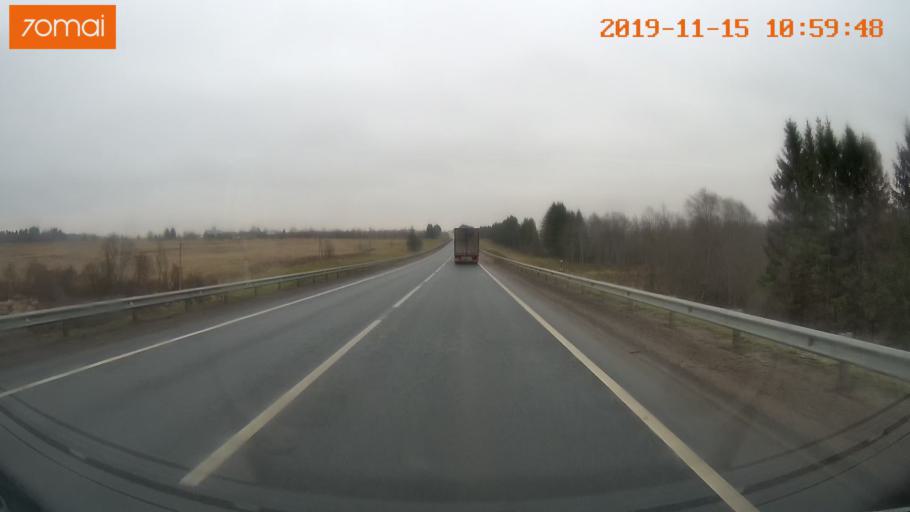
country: RU
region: Vologda
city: Chebsara
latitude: 59.1400
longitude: 38.8854
